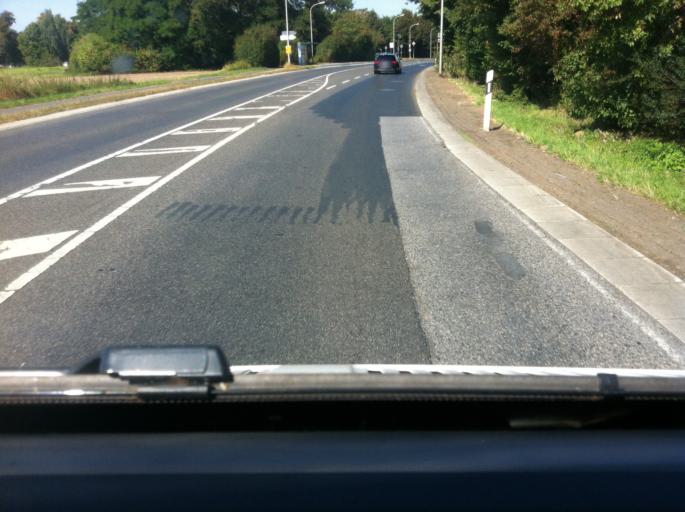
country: DE
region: North Rhine-Westphalia
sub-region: Regierungsbezirk Koln
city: Pulheim
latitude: 50.9588
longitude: 6.7999
